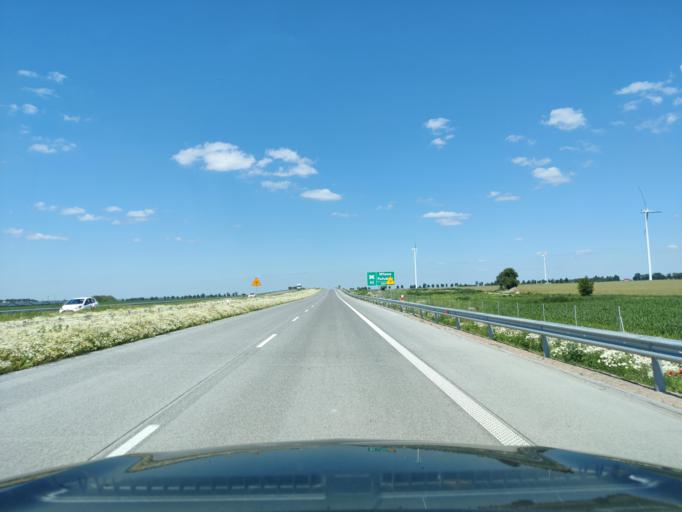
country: PL
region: Masovian Voivodeship
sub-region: Powiat mlawski
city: Wisniewo
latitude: 53.0454
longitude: 20.3591
